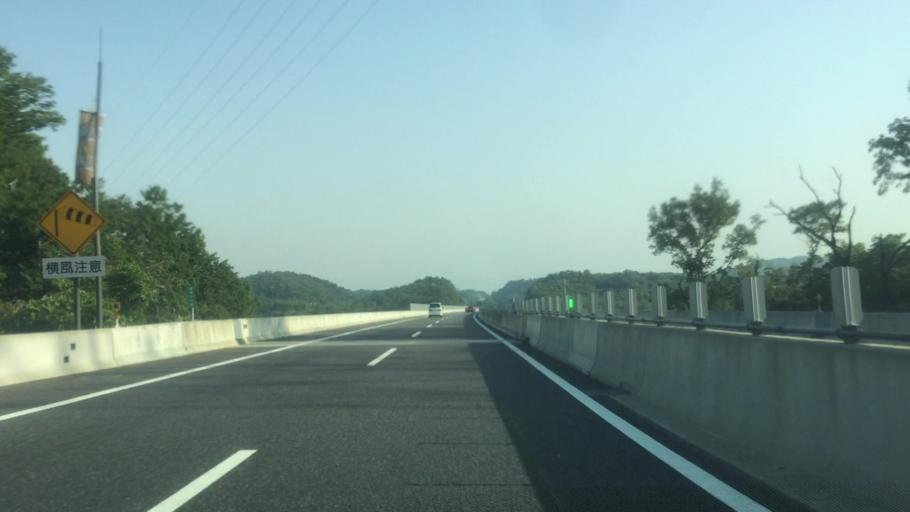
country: JP
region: Aichi
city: Okazaki
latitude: 34.9945
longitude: 137.2328
